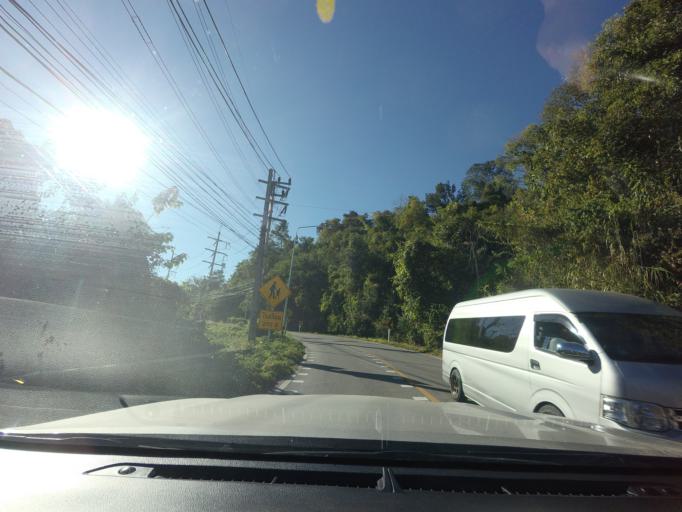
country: TH
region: Mae Hong Son
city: Mae Hi
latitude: 19.2050
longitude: 98.6744
